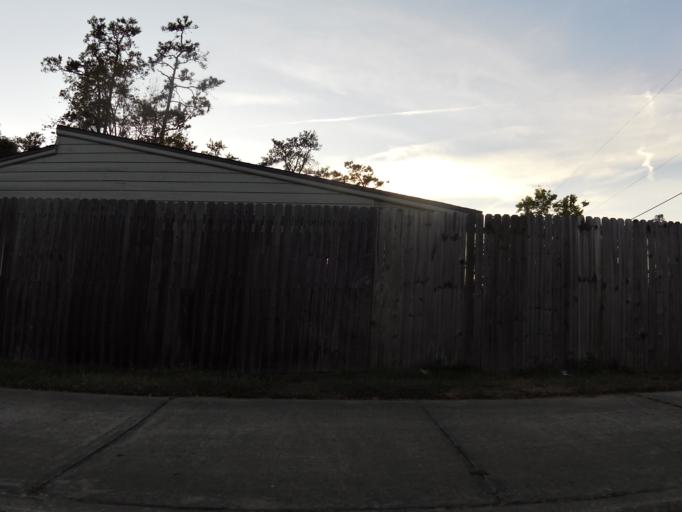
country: US
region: Florida
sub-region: Duval County
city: Jacksonville
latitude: 30.2936
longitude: -81.6439
